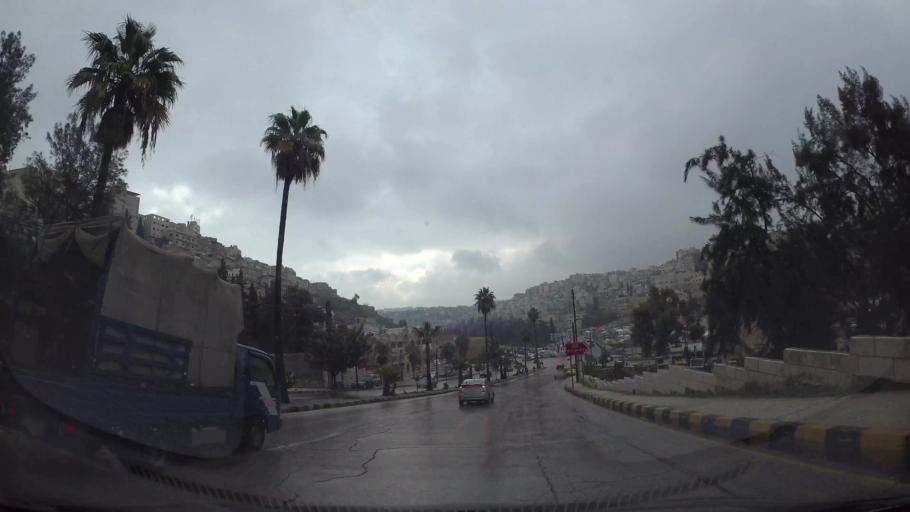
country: JO
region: Amman
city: Amman
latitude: 31.9492
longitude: 35.9146
